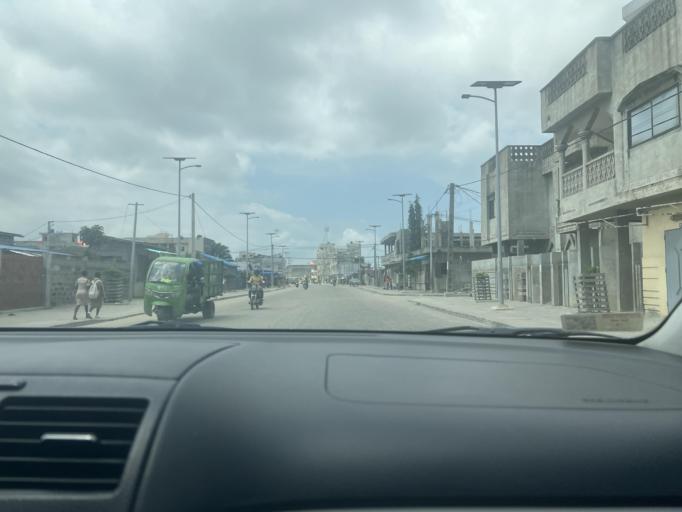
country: BJ
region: Littoral
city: Cotonou
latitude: 6.3893
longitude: 2.4509
